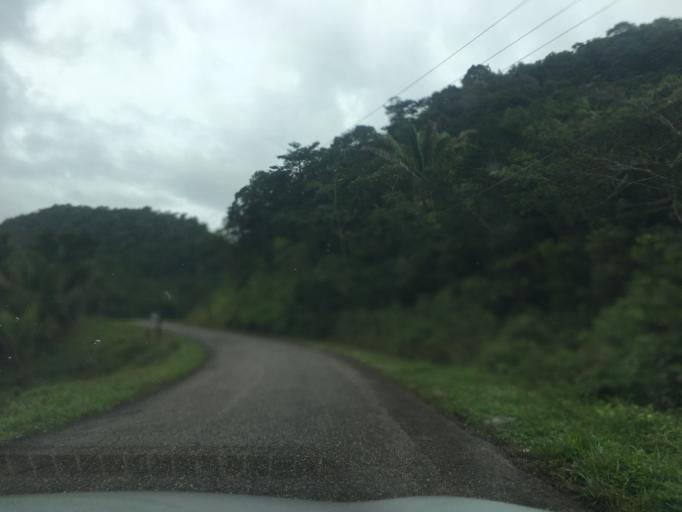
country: BZ
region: Cayo
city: Belmopan
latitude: 17.0596
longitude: -88.5869
